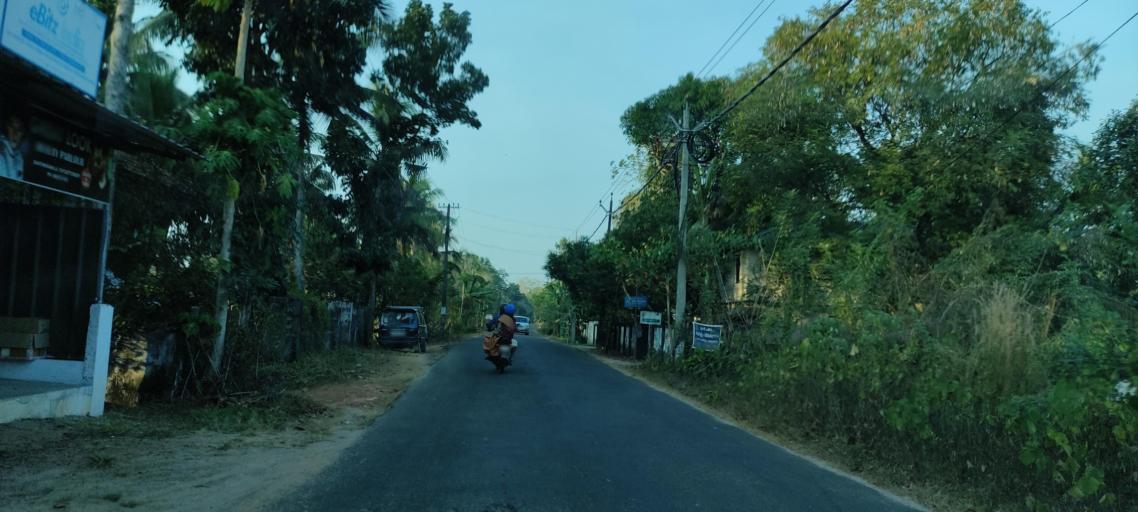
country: IN
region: Kerala
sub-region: Alappuzha
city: Kutiatodu
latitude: 9.7638
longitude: 76.3533
